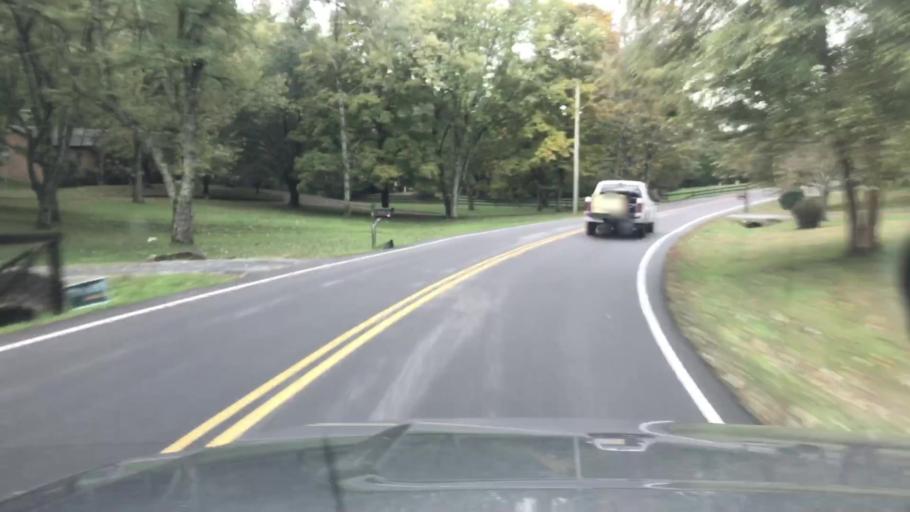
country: US
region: Tennessee
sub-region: Williamson County
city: Brentwood Estates
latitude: 35.9883
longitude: -86.8286
